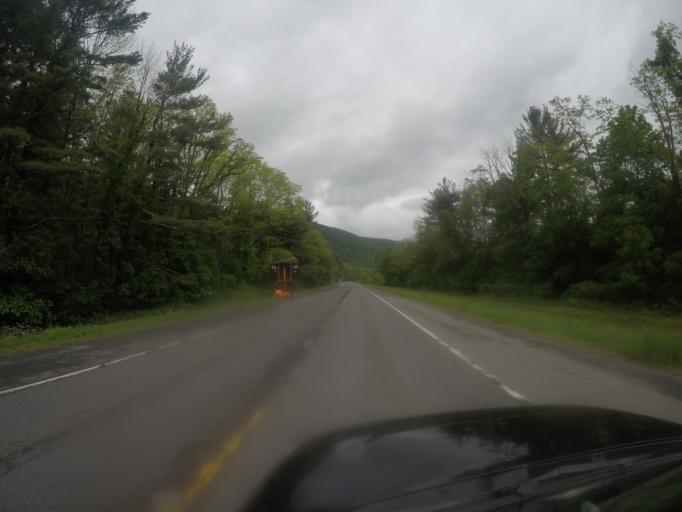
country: US
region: New York
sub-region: Ulster County
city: Shokan
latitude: 42.0559
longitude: -74.2980
